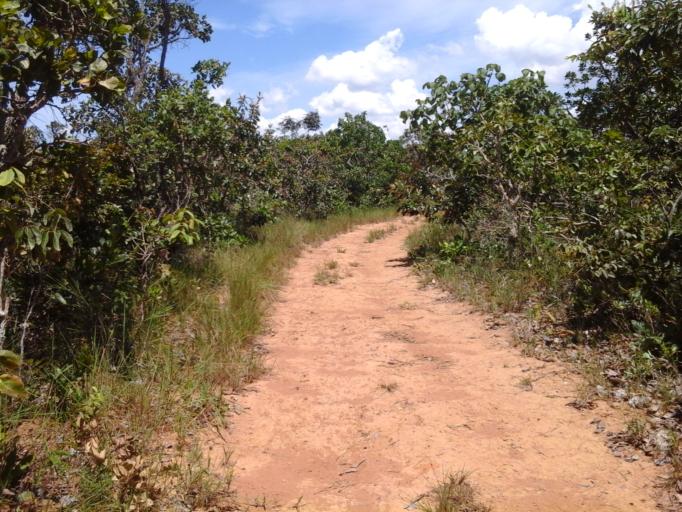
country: BR
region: Goias
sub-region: Abadiania
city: Abadiania
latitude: -15.9758
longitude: -48.5334
